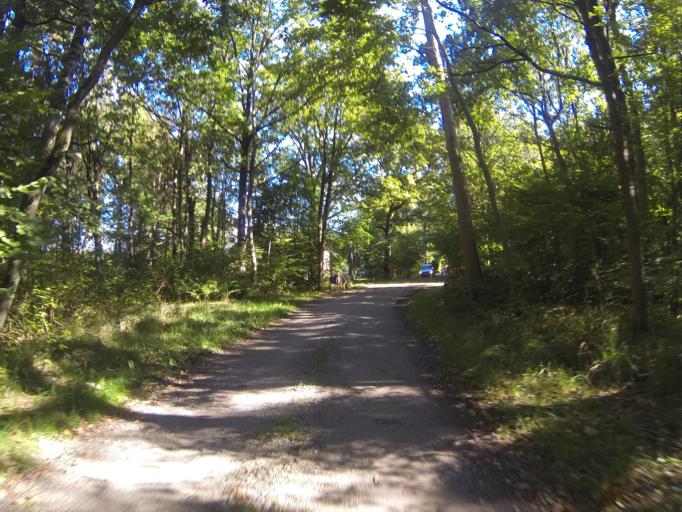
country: SE
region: Skane
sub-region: Hoors Kommun
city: Loberod
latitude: 55.7346
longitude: 13.3954
